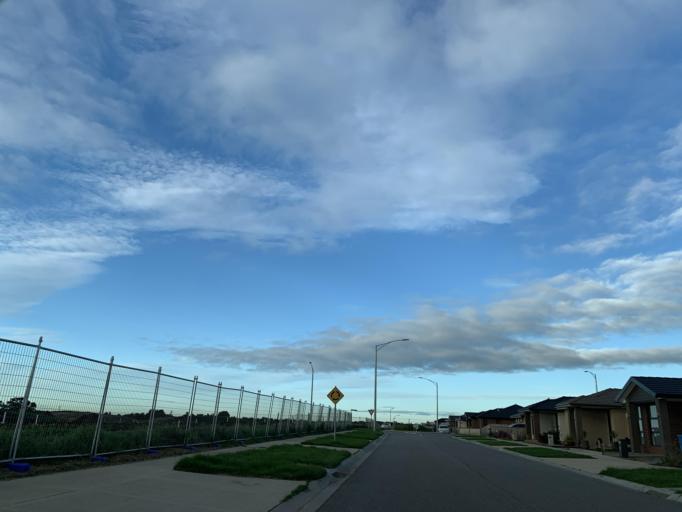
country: AU
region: Victoria
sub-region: Casey
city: Junction Village
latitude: -38.1282
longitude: 145.3080
